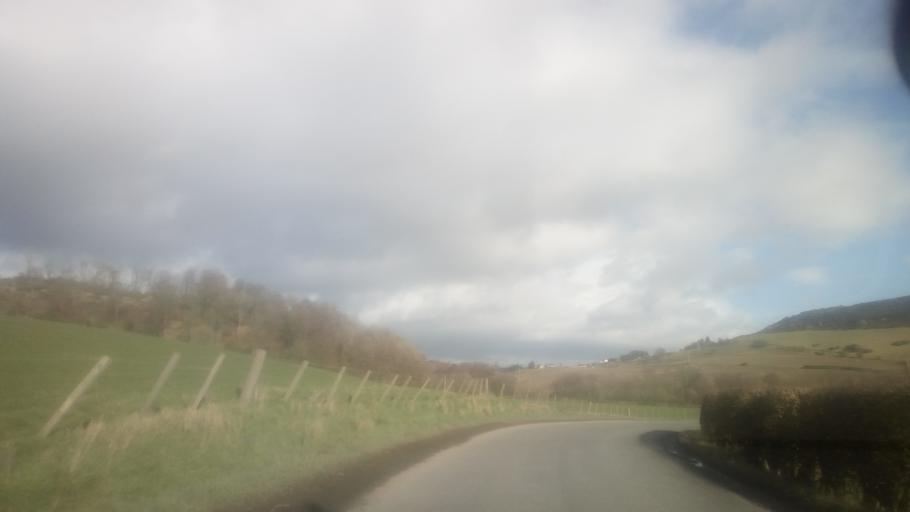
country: GB
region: Scotland
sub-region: The Scottish Borders
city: Hawick
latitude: 55.4129
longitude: -2.8244
